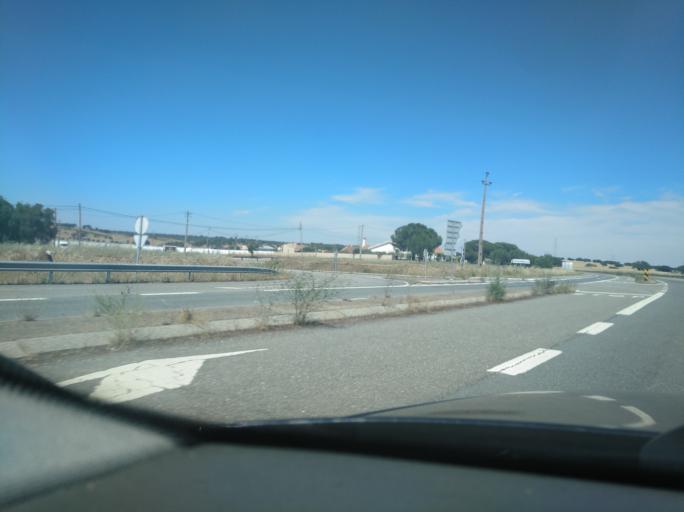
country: PT
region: Beja
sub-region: Ourique
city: Ourique
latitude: 37.6622
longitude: -8.1774
